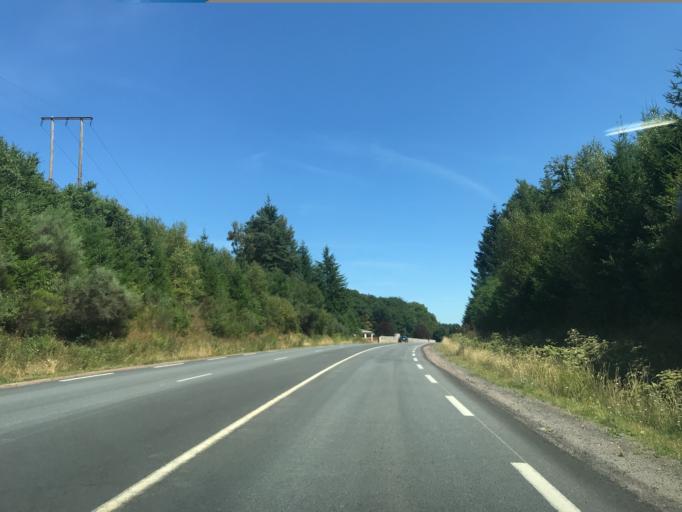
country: FR
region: Limousin
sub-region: Departement de la Correze
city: Egletons
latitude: 45.4398
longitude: 2.0959
